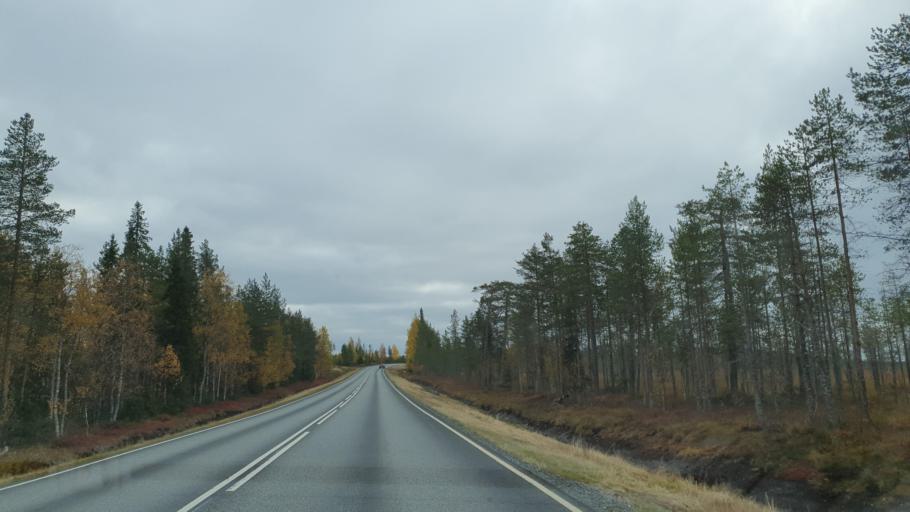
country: FI
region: Lapland
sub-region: Rovaniemi
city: Ranua
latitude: 65.8049
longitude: 26.5650
